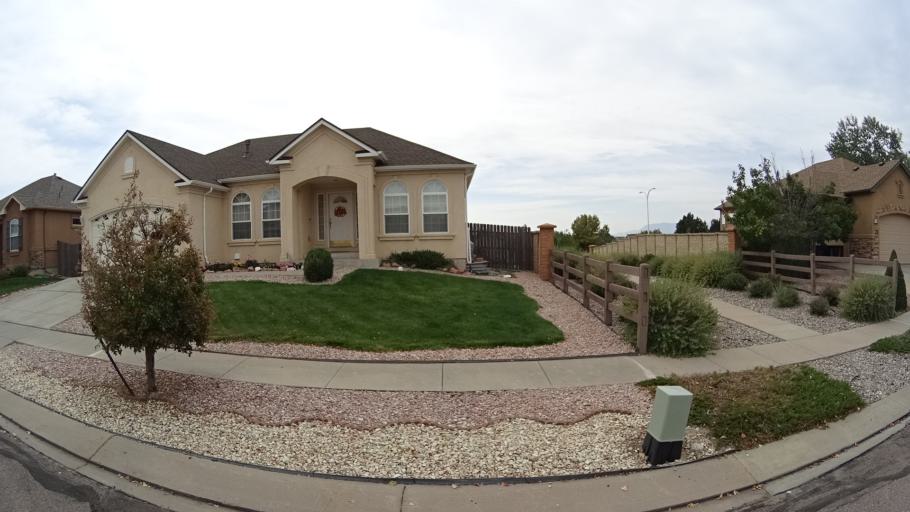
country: US
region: Colorado
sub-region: El Paso County
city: Cimarron Hills
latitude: 38.9124
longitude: -104.6888
